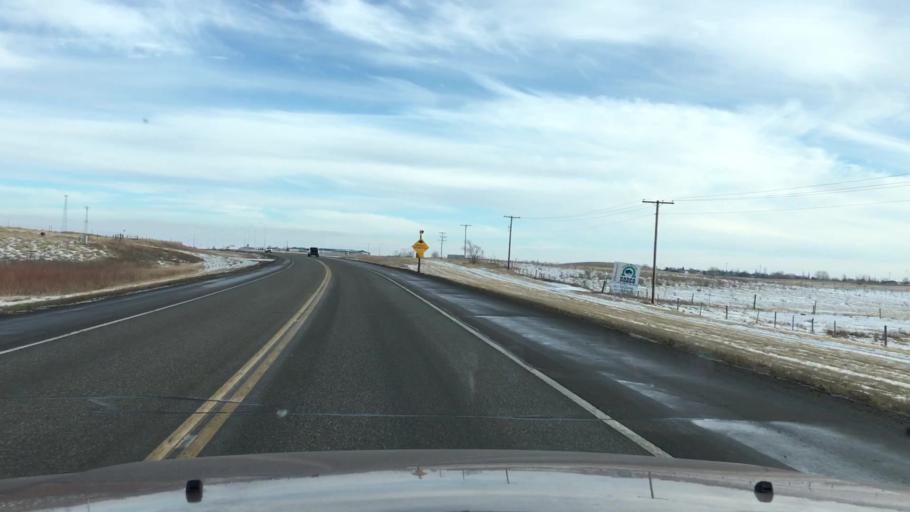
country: CA
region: Saskatchewan
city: Pilot Butte
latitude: 50.4844
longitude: -104.4431
